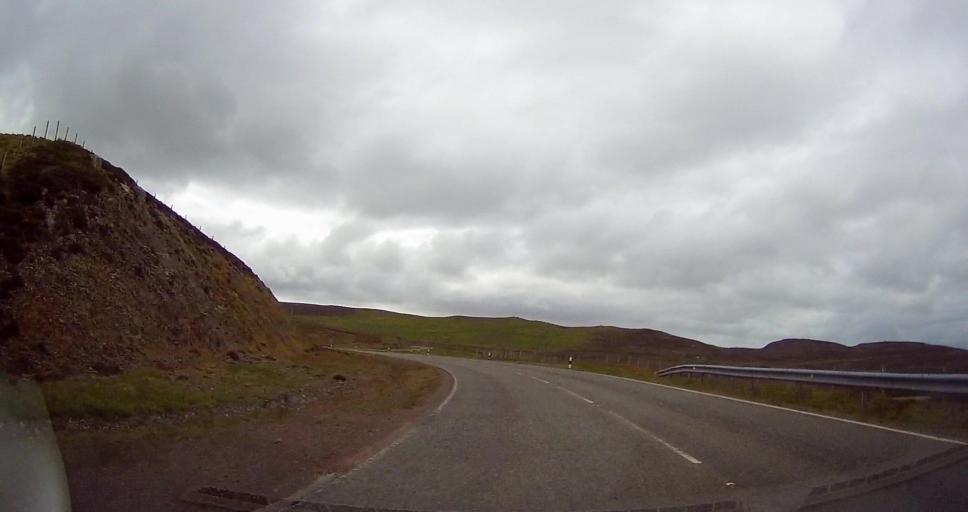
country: GB
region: Scotland
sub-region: Shetland Islands
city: Sandwick
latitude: 60.2589
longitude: -1.4827
